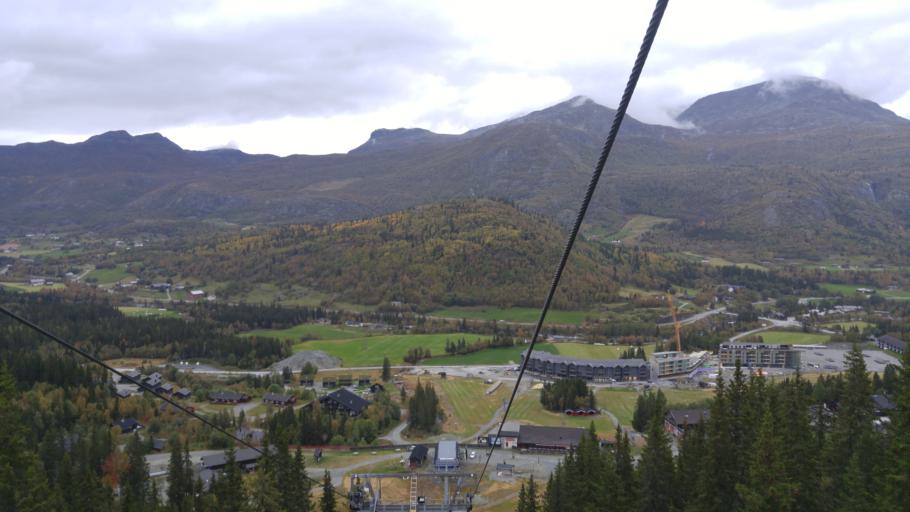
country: NO
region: Buskerud
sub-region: Hemsedal
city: Hemsedal
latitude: 60.8578
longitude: 8.5131
